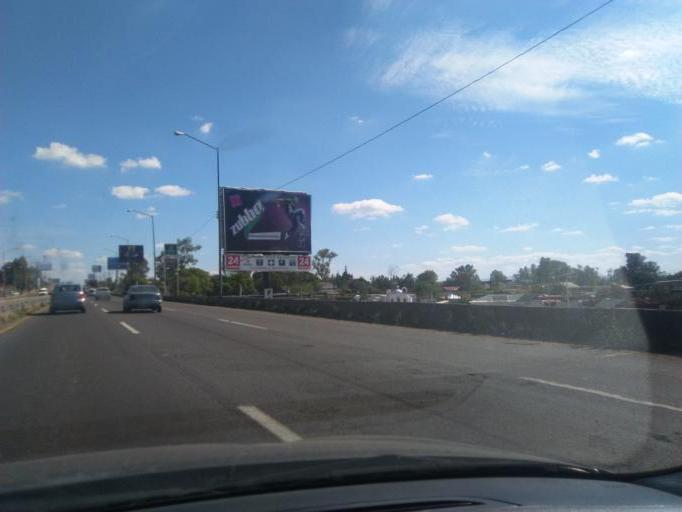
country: MX
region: Guanajuato
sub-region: Leon
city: Ladrilleras del Refugio
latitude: 21.0447
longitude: -101.5642
